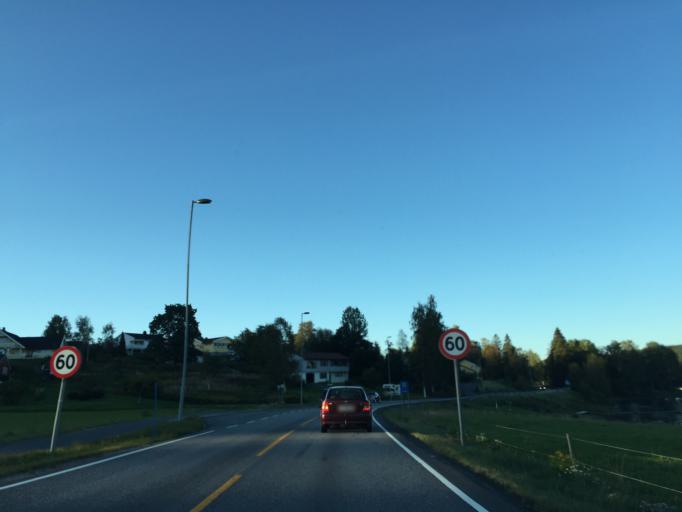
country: NO
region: Hedmark
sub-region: Nord-Odal
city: Sand
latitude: 60.3834
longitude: 11.5393
